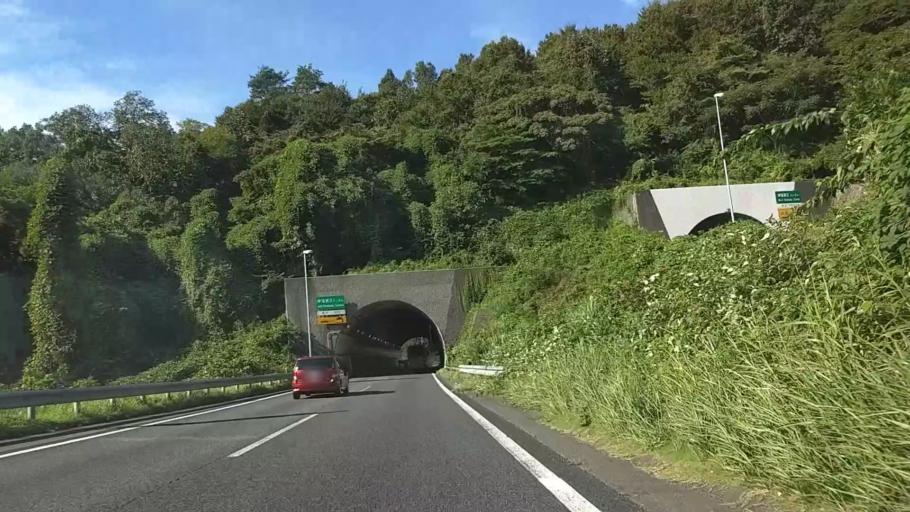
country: JP
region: Yamanashi
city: Uenohara
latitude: 35.6148
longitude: 139.0304
